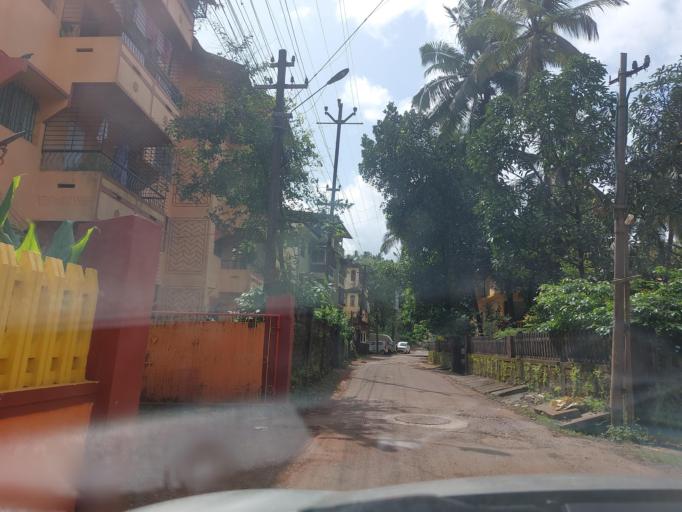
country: IN
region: Goa
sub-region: North Goa
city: Queula
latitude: 15.3980
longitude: 73.9998
